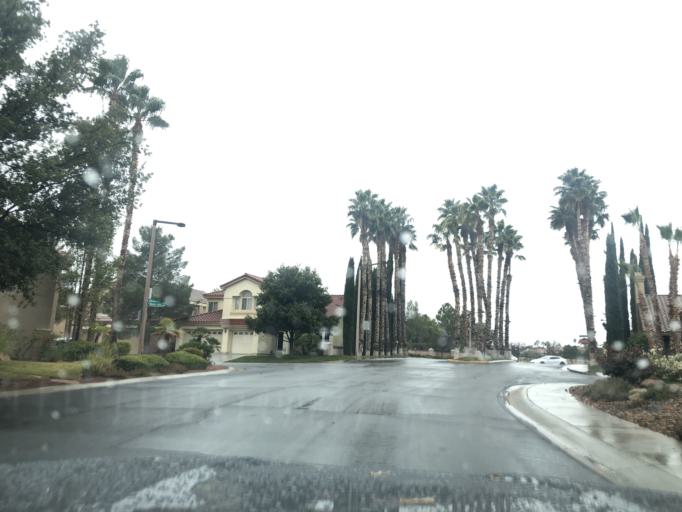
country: US
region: Nevada
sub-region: Clark County
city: Summerlin South
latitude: 36.1980
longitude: -115.2889
